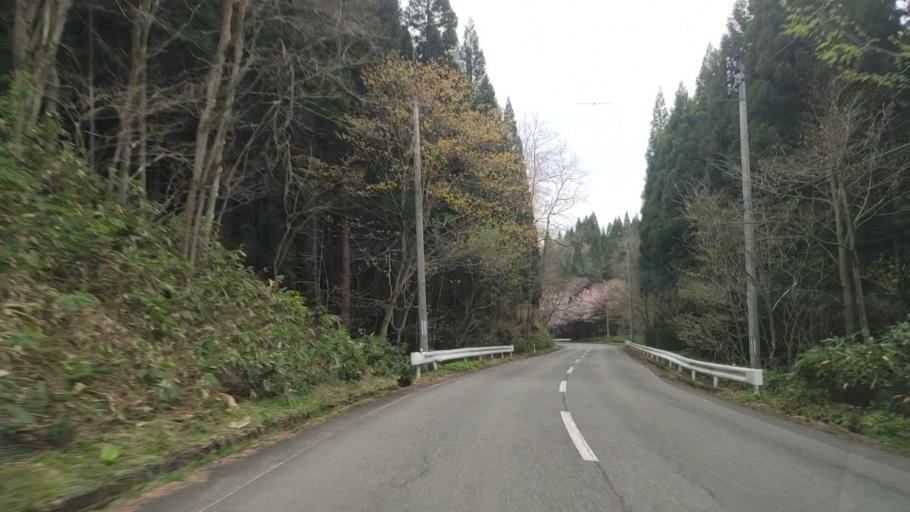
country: JP
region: Akita
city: Hanawa
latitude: 40.3674
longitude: 140.7851
